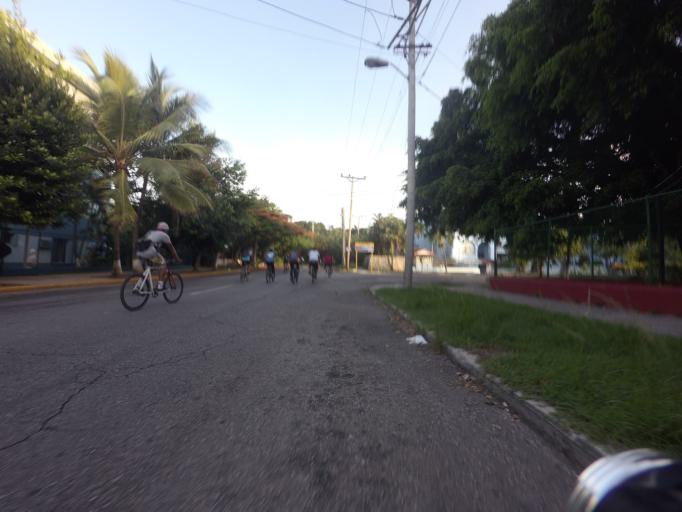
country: CU
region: La Habana
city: Havana
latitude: 23.1199
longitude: -82.4120
